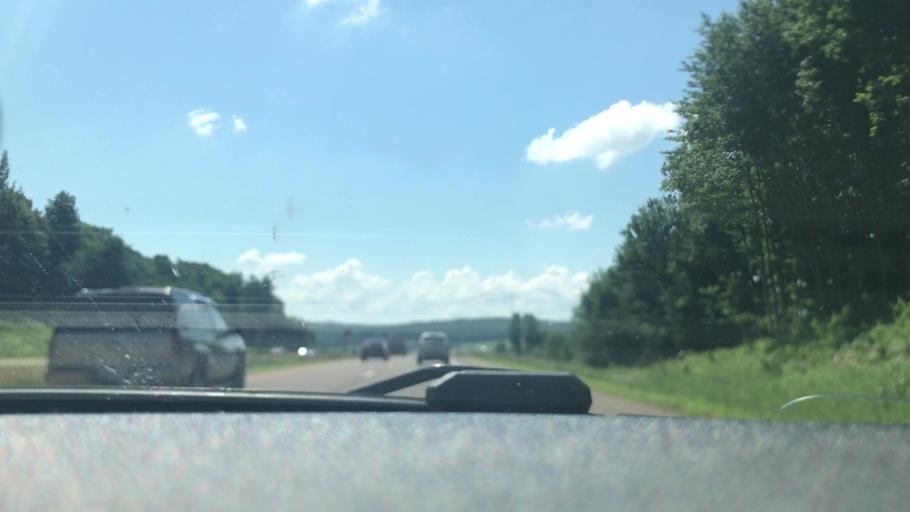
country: US
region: Wisconsin
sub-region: Chippewa County
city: Chippewa Falls
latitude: 44.9745
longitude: -91.4341
